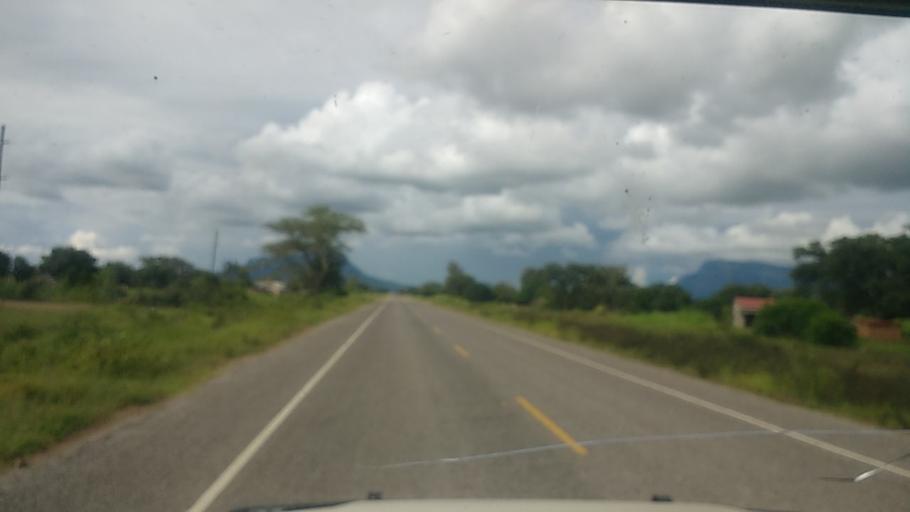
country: UG
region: Eastern Region
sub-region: Katakwi District
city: Katakwi
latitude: 2.0273
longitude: 34.1221
